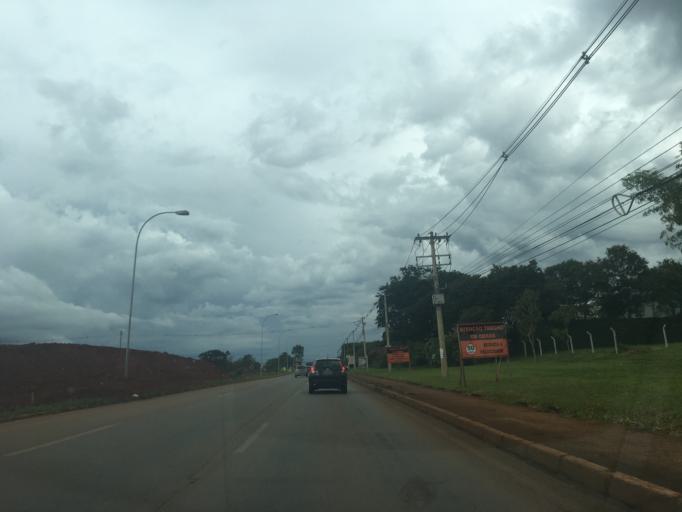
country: BR
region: Federal District
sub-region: Brasilia
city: Brasilia
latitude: -15.7275
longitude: -47.8949
